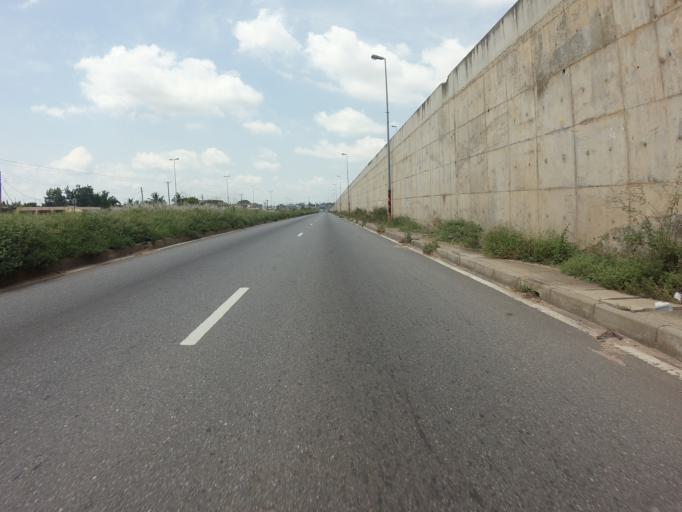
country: GH
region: Greater Accra
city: Gbawe
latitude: 5.6246
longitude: -0.3044
